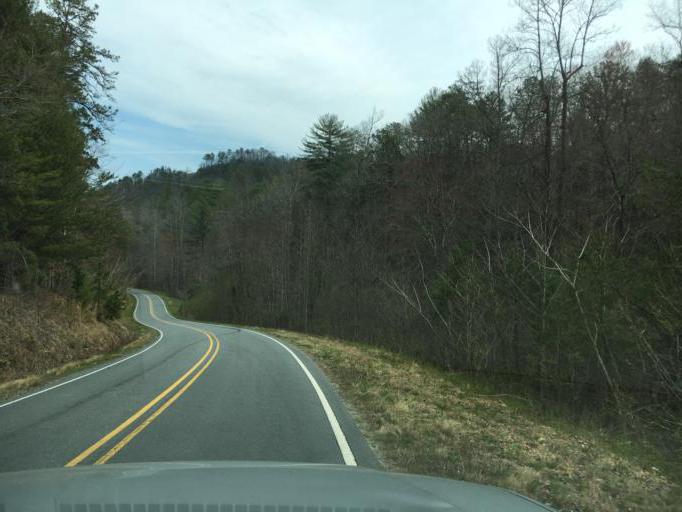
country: US
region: North Carolina
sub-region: Rutherford County
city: Lake Lure
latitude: 35.4046
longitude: -82.1906
